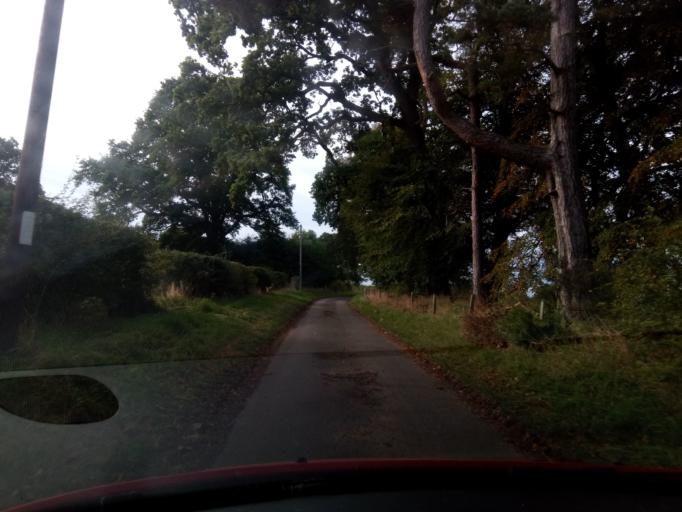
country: GB
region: Scotland
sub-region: The Scottish Borders
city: Kelso
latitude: 55.5918
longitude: -2.3944
